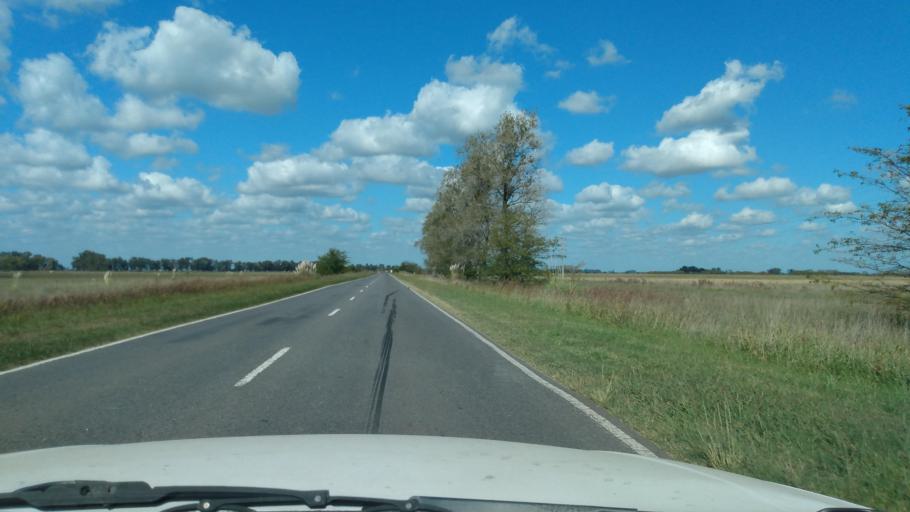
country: AR
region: Buenos Aires
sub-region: Partido de Navarro
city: Navarro
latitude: -34.8693
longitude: -59.3422
